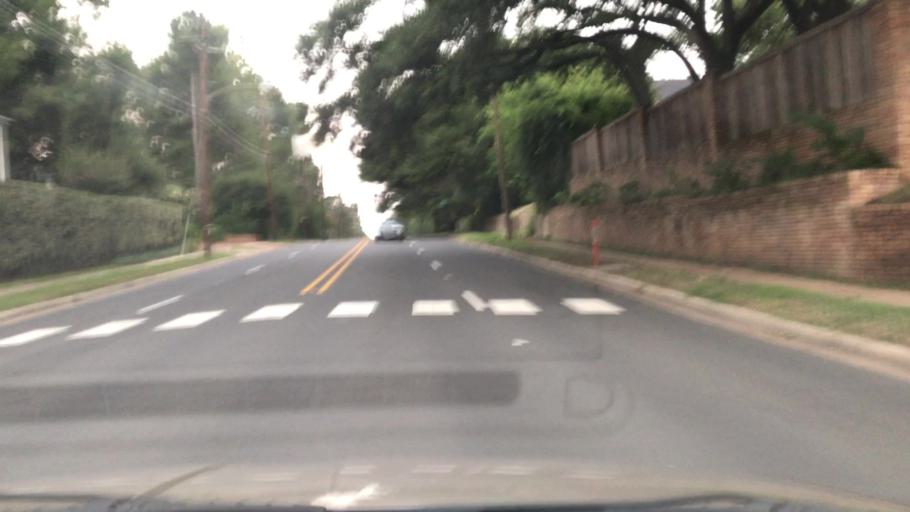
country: US
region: Louisiana
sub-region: Bossier Parish
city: Bossier City
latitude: 32.4607
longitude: -93.7460
